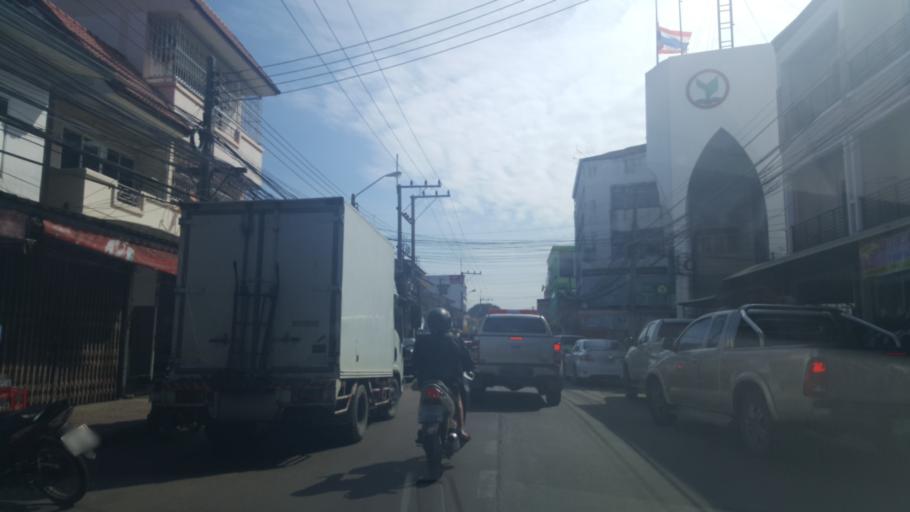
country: TH
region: Chon Buri
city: Sattahip
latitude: 12.6652
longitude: 100.9018
